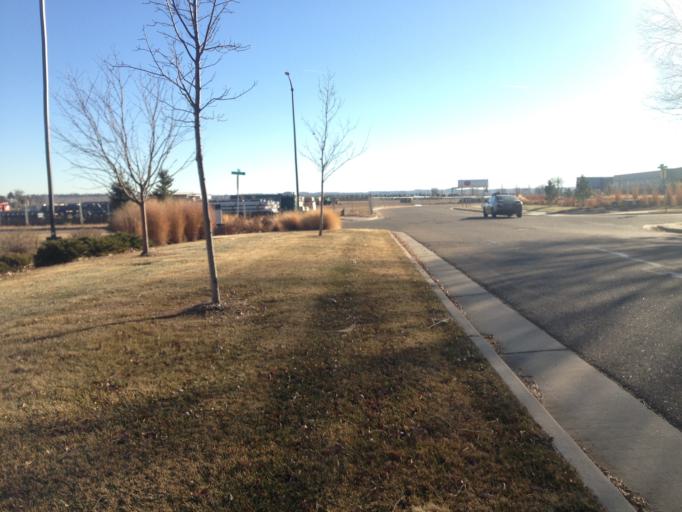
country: US
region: Colorado
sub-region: Boulder County
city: Louisville
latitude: 39.9632
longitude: -105.1121
